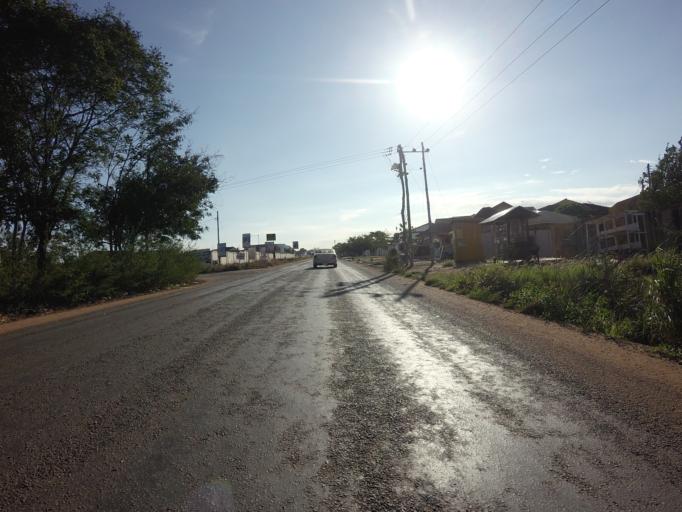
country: GH
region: Greater Accra
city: Nungua
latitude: 5.6502
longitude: -0.0720
